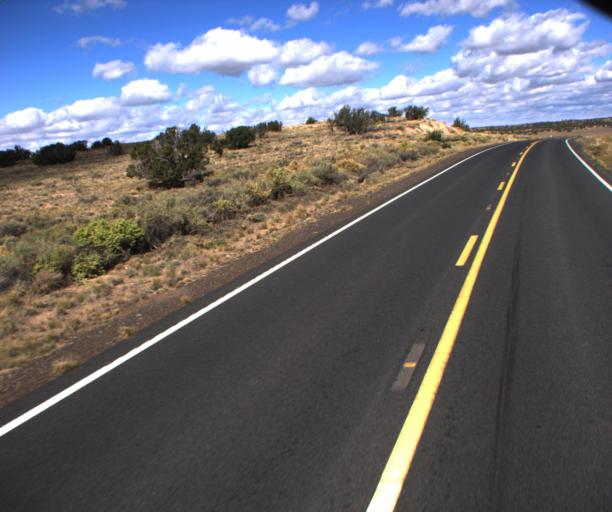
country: US
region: Arizona
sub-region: Apache County
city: Houck
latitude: 35.0873
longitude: -109.3104
